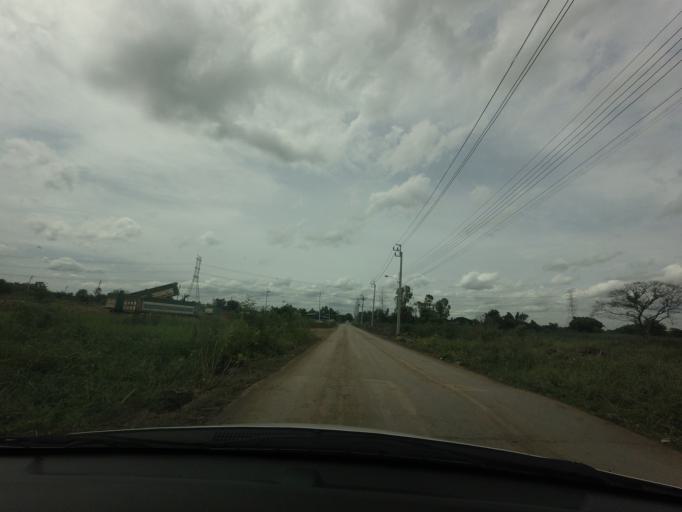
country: TH
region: Bangkok
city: Min Buri
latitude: 13.7841
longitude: 100.7613
